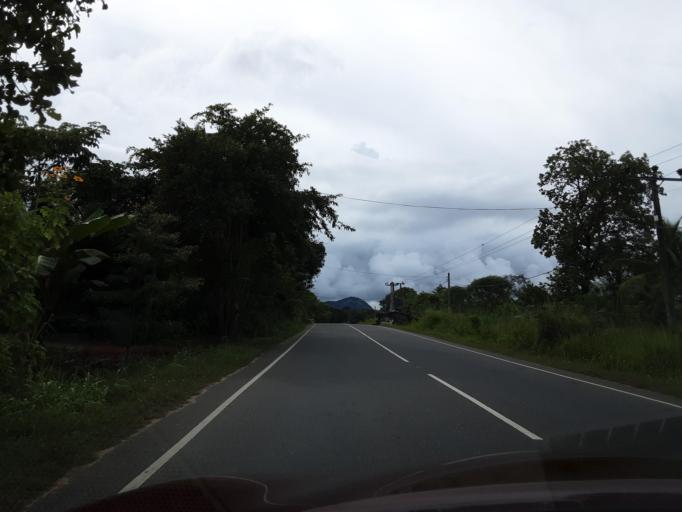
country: LK
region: Uva
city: Badulla
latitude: 7.3876
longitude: 81.1485
